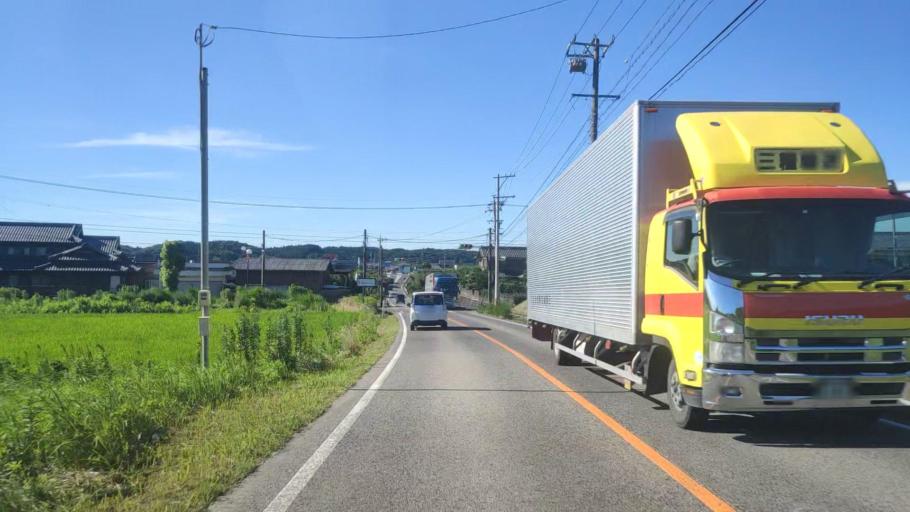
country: JP
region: Mie
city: Ueno-ebisumachi
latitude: 34.8333
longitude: 136.2363
